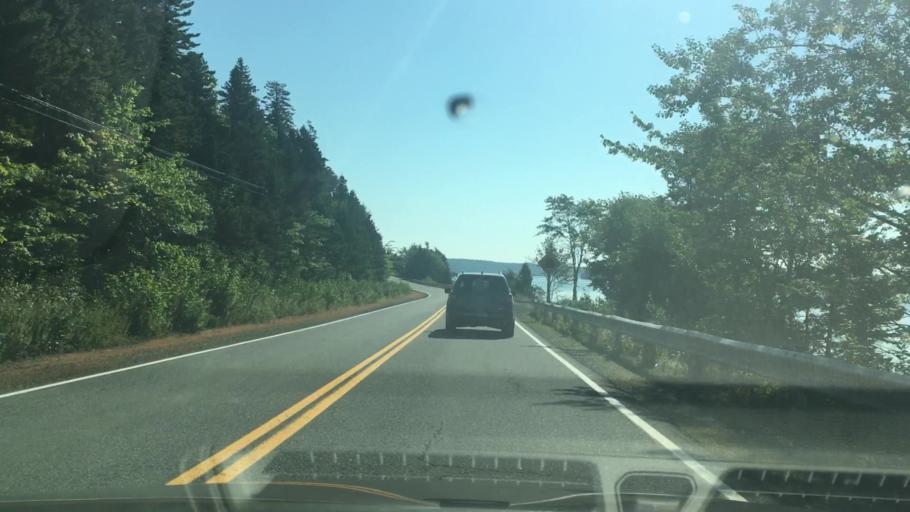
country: CA
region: Nova Scotia
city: Cole Harbour
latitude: 44.8148
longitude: -62.8754
